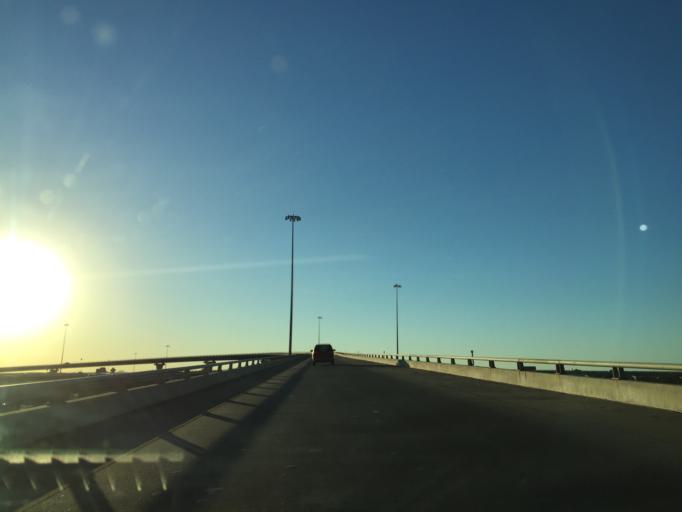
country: US
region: Texas
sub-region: Travis County
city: Austin
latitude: 30.3224
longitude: -97.7028
